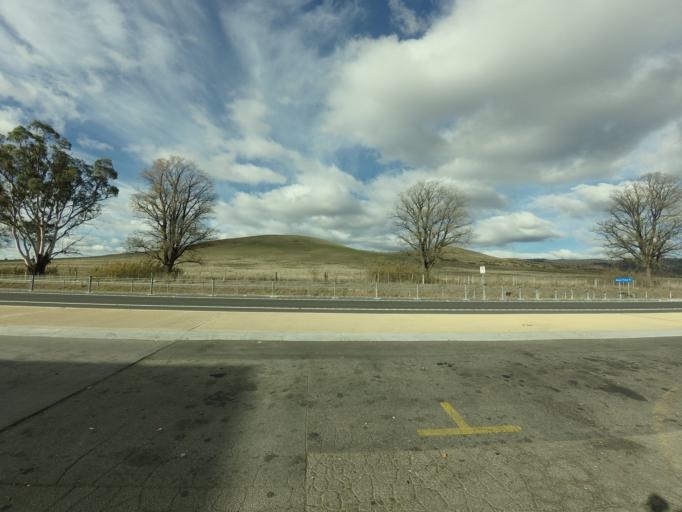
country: AU
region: Tasmania
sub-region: Brighton
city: Bridgewater
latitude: -42.5134
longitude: 147.1893
